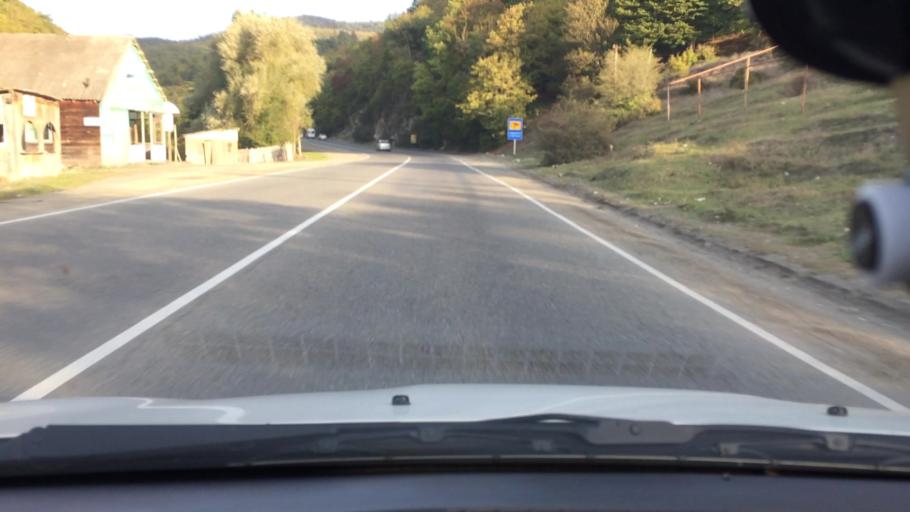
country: GE
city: Surami
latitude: 42.0352
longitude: 43.5207
